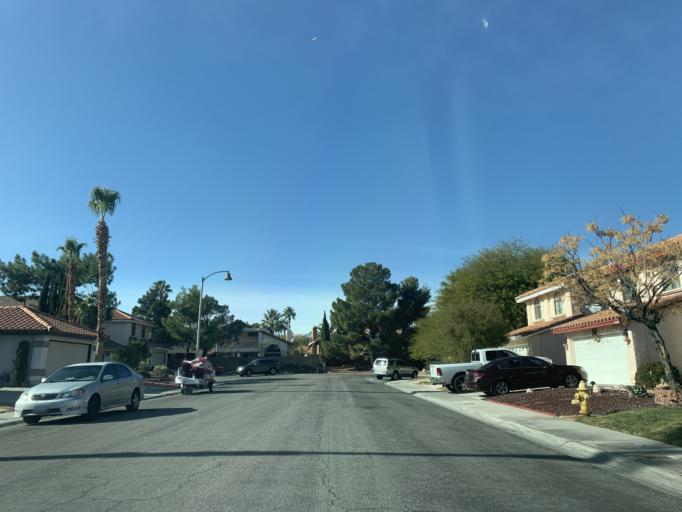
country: US
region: Nevada
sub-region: Clark County
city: Summerlin South
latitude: 36.1352
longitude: -115.2940
